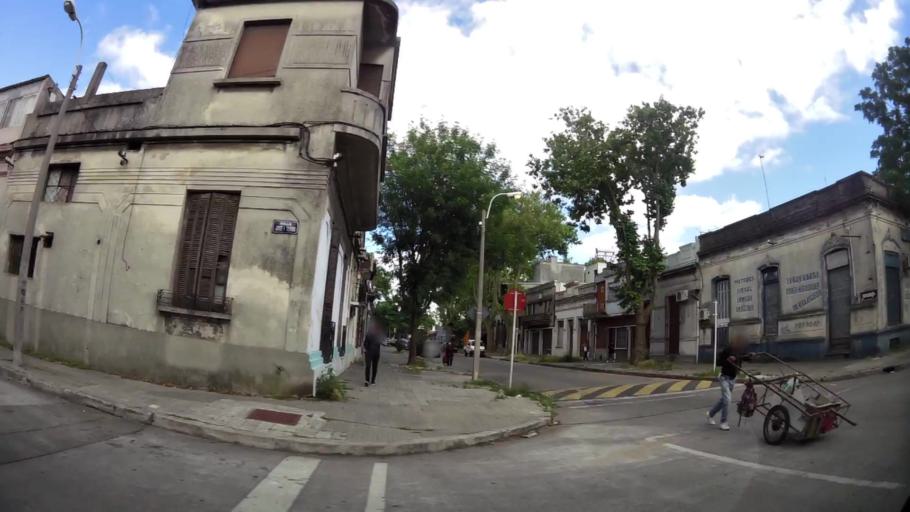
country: UY
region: Montevideo
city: Montevideo
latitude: -34.8802
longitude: -56.1804
